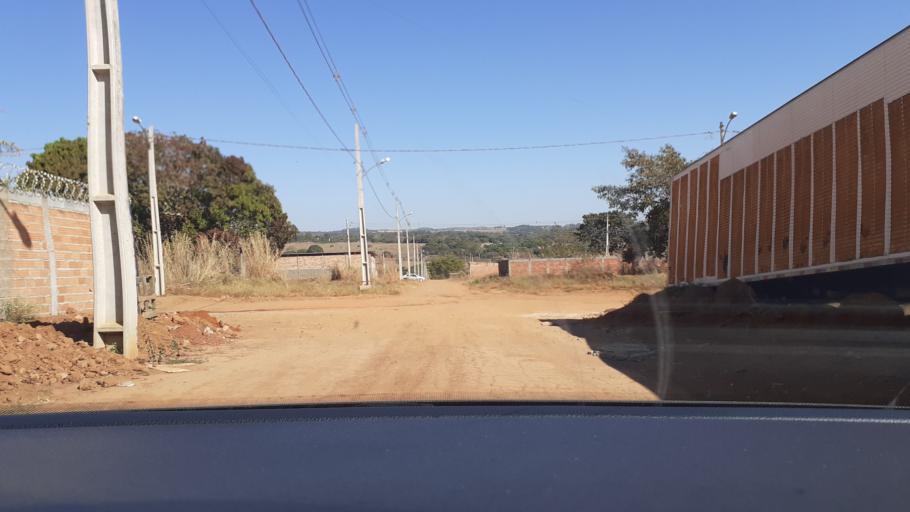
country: BR
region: Goias
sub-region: Aparecida De Goiania
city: Aparecida de Goiania
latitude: -16.8919
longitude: -49.2580
